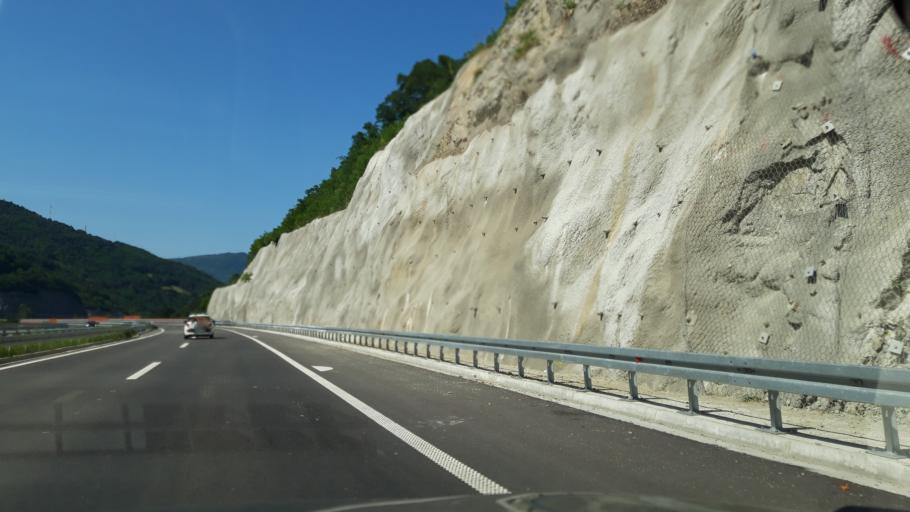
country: RS
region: Central Serbia
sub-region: Pcinjski Okrug
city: Vladicin Han
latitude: 42.7622
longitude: 22.0862
